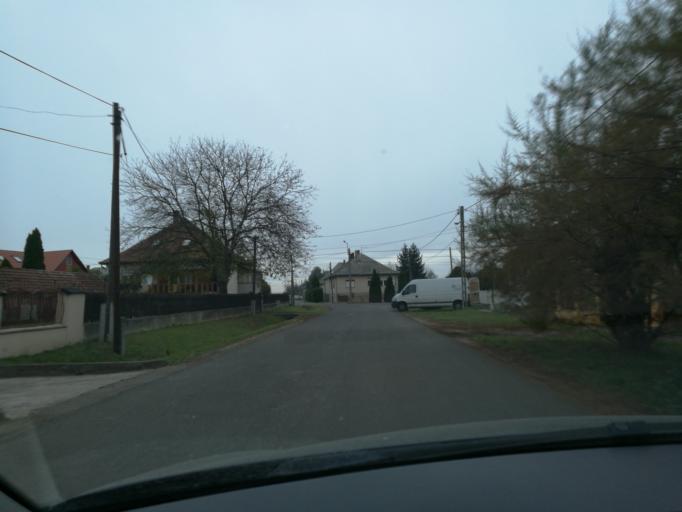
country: HU
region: Nograd
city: Szecseny
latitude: 48.0747
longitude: 19.5287
